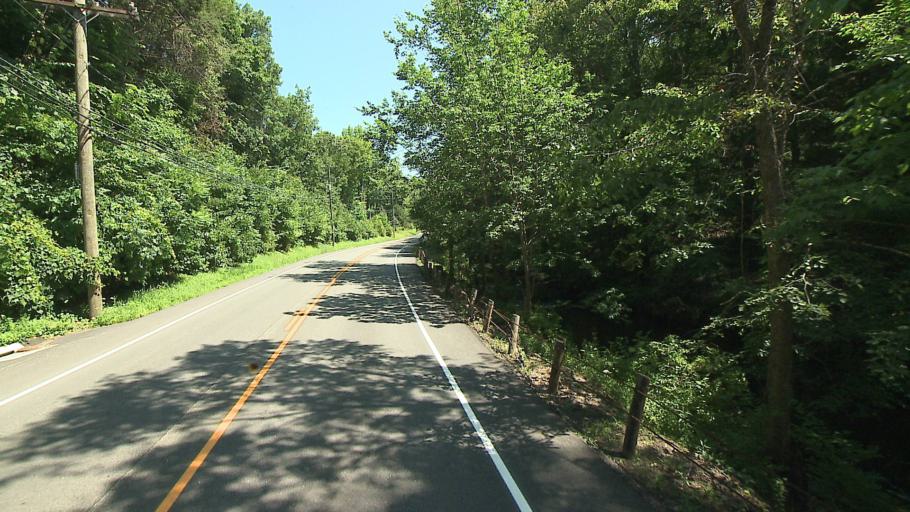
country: US
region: Connecticut
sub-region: Litchfield County
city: New Preston
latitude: 41.8289
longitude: -73.3531
